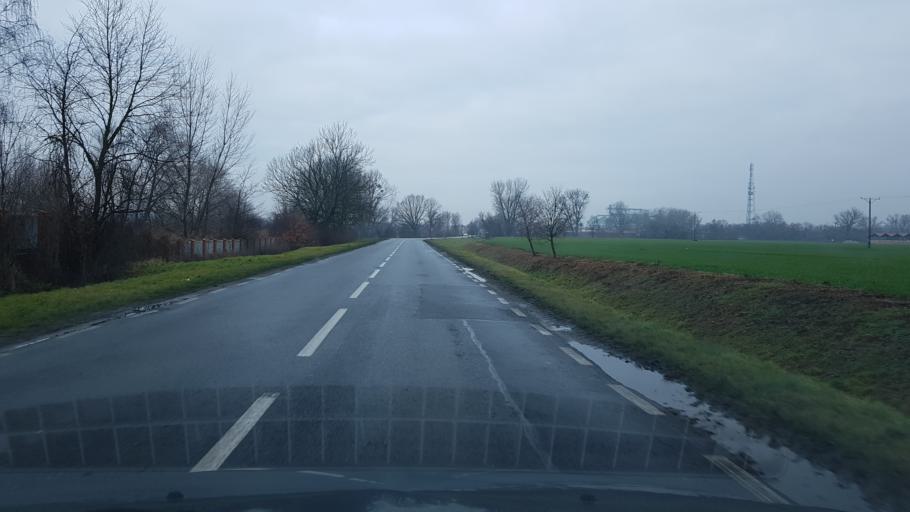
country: PL
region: Lower Silesian Voivodeship
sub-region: Powiat wroclawski
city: Zorawina
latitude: 50.9848
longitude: 17.0230
